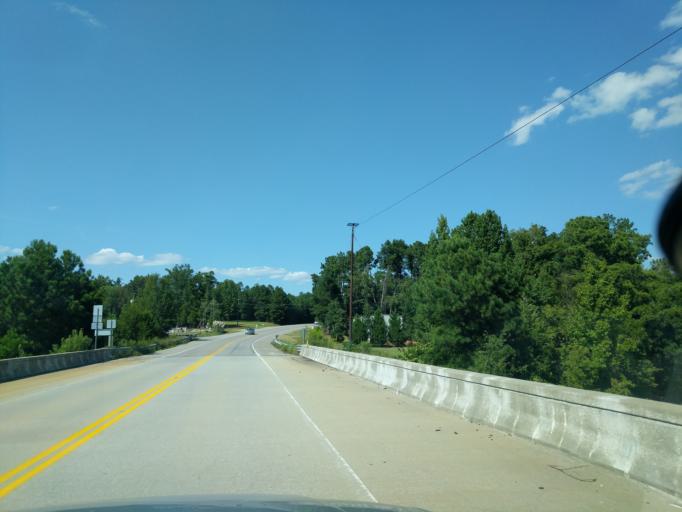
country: US
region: South Carolina
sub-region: Newberry County
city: Prosperity
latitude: 34.1008
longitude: -81.5685
